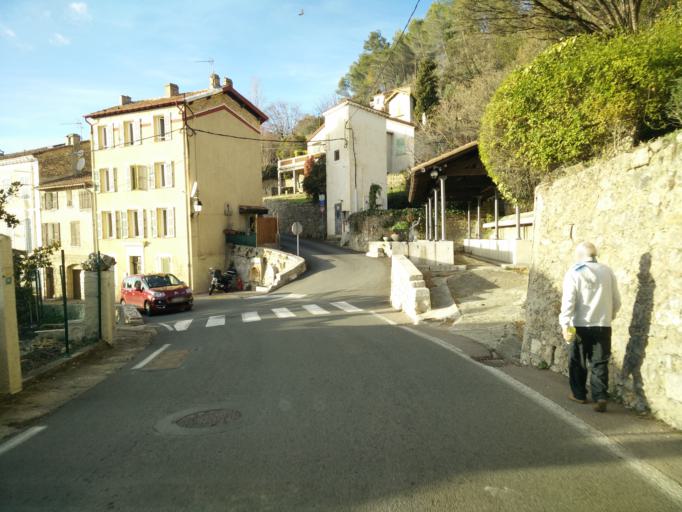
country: FR
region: Provence-Alpes-Cote d'Azur
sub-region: Departement du Var
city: Callian
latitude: 43.6238
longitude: 6.7520
